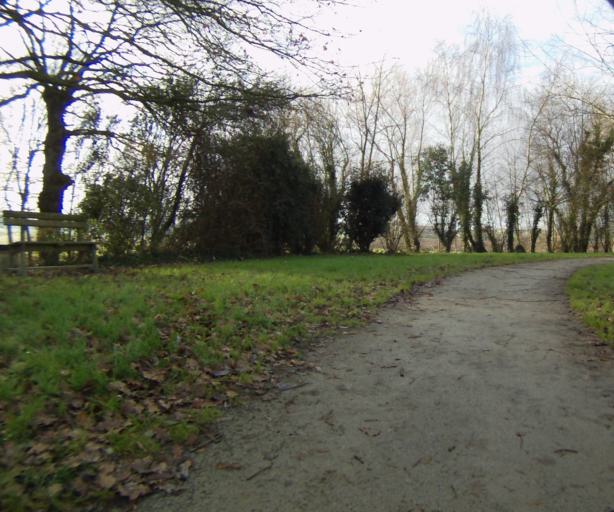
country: FR
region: Brittany
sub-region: Departement d'Ille-et-Vilaine
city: Janze
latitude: 47.9523
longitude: -1.5326
